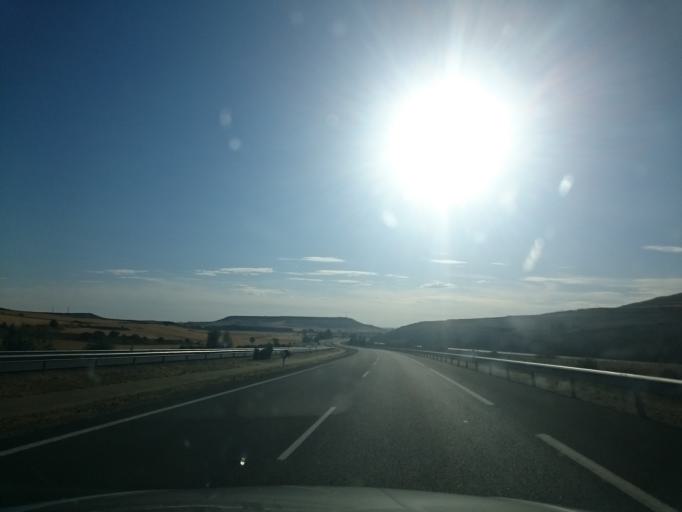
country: ES
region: Castille and Leon
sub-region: Provincia de Burgos
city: Sasamon
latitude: 42.3946
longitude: -4.0065
